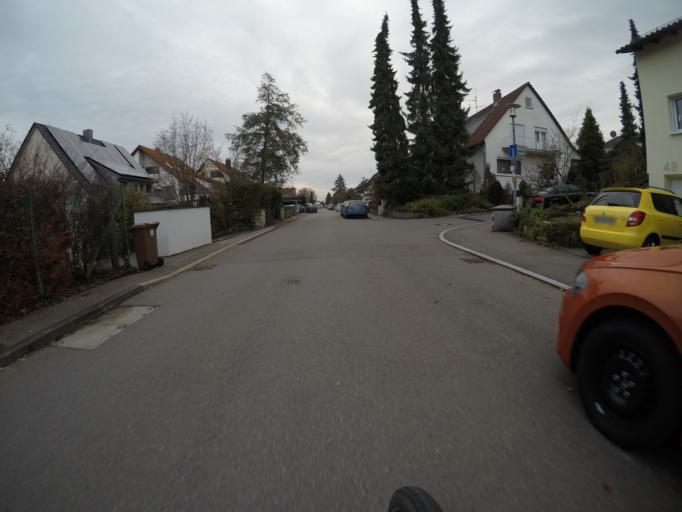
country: DE
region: Baden-Wuerttemberg
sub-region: Regierungsbezirk Stuttgart
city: Steinenbronn
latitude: 48.7077
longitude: 9.1135
